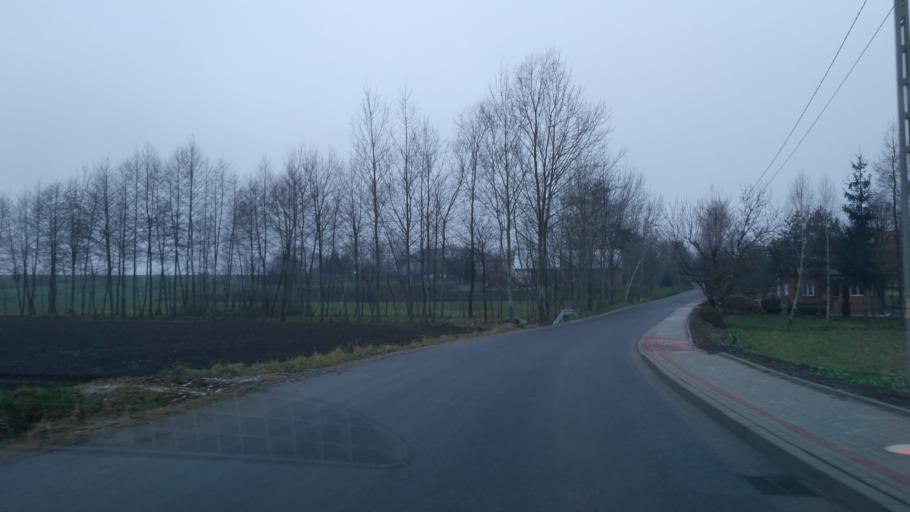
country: PL
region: Subcarpathian Voivodeship
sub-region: Powiat przeworski
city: Kanczuga
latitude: 50.0146
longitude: 22.4167
